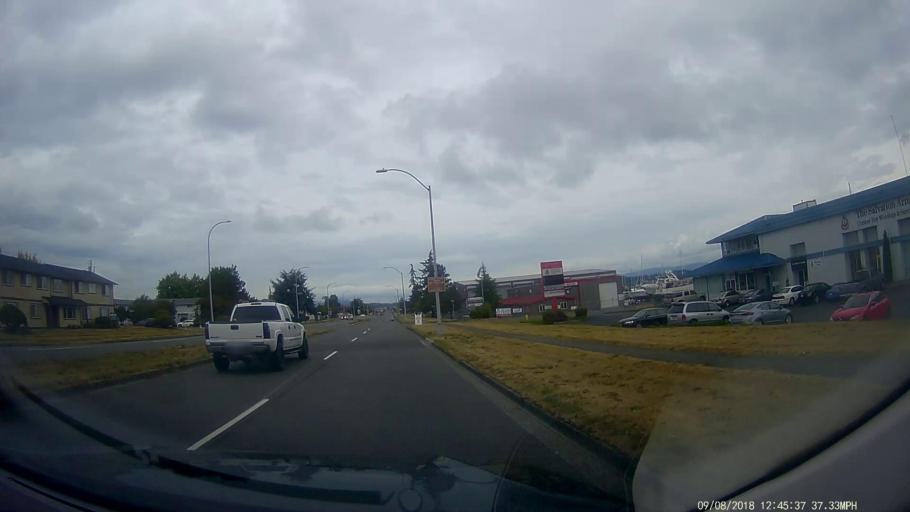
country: US
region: Washington
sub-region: Skagit County
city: Anacortes
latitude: 48.4972
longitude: -122.6092
